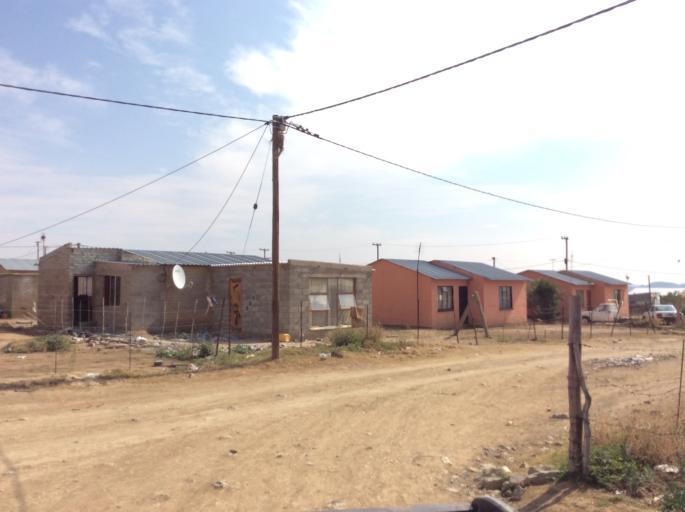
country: ZA
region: Orange Free State
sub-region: Xhariep District Municipality
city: Dewetsdorp
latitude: -29.5948
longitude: 26.6832
